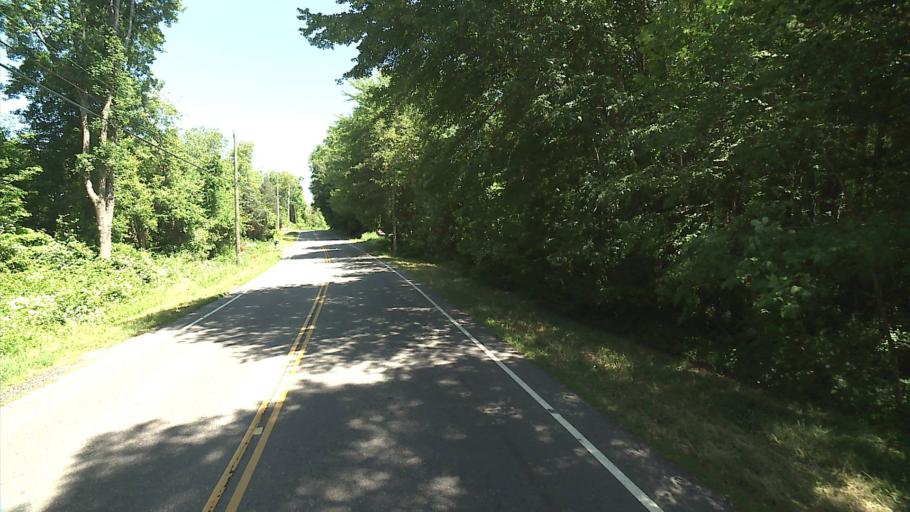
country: US
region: Rhode Island
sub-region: Washington County
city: Hopkinton
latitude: 41.4758
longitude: -71.8320
